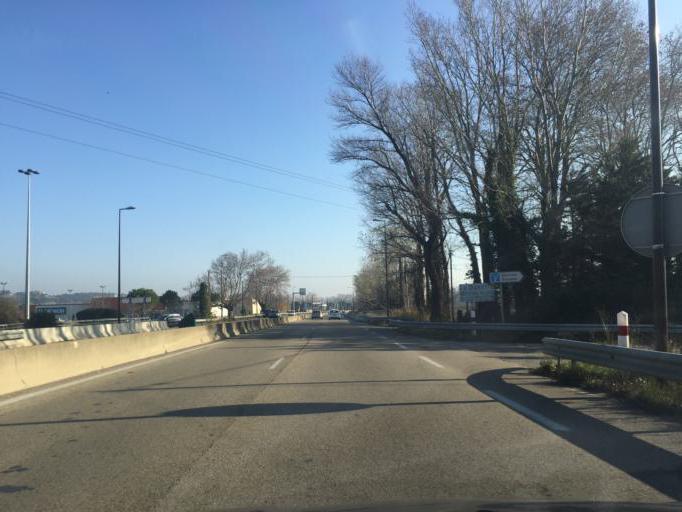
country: FR
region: Provence-Alpes-Cote d'Azur
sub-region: Departement du Vaucluse
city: Montfavet
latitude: 43.9197
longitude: 4.8645
